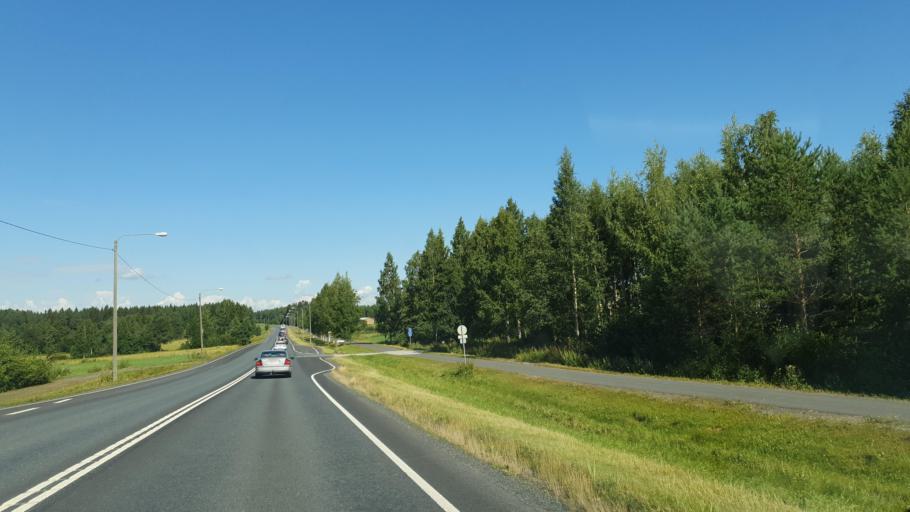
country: FI
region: Northern Savo
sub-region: Ylae-Savo
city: Lapinlahti
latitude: 63.4328
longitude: 27.3271
